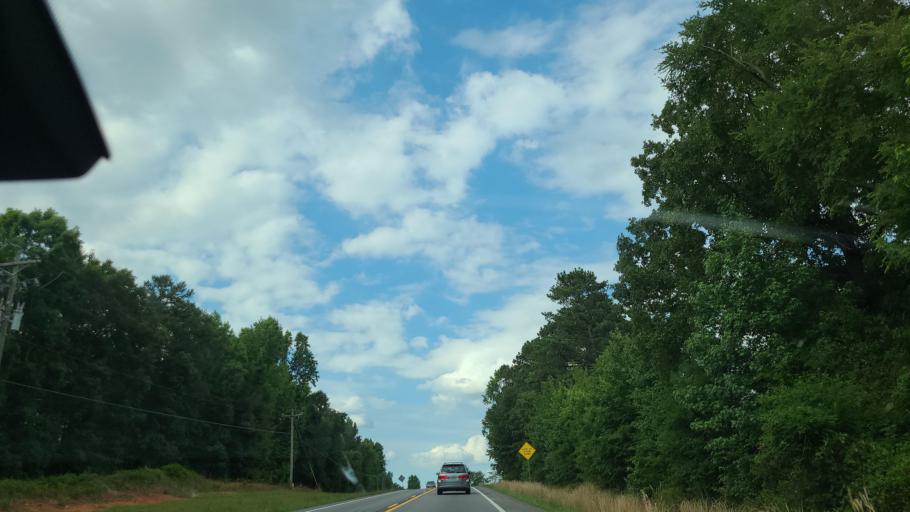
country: US
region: Georgia
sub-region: Putnam County
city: Eatonton
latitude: 33.2397
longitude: -83.4334
